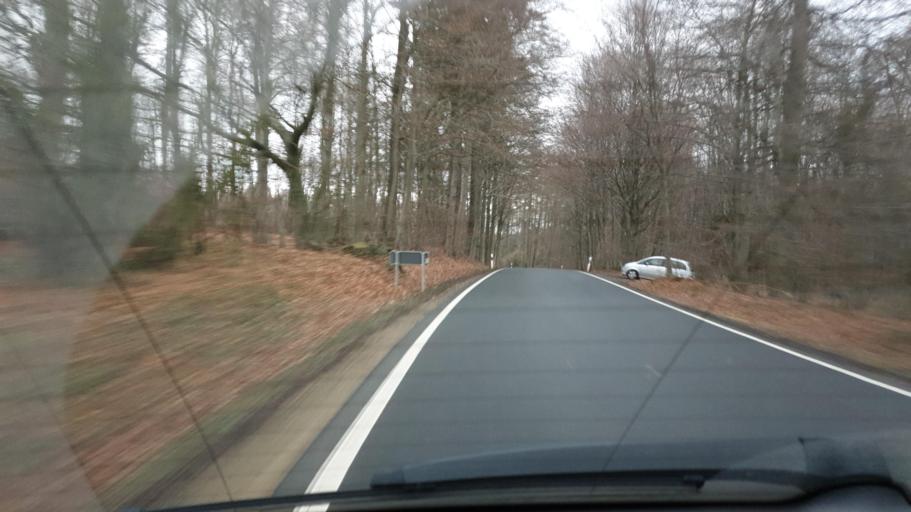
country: DE
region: North Rhine-Westphalia
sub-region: Regierungsbezirk Detmold
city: Lemgo
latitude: 52.0617
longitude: 8.8541
